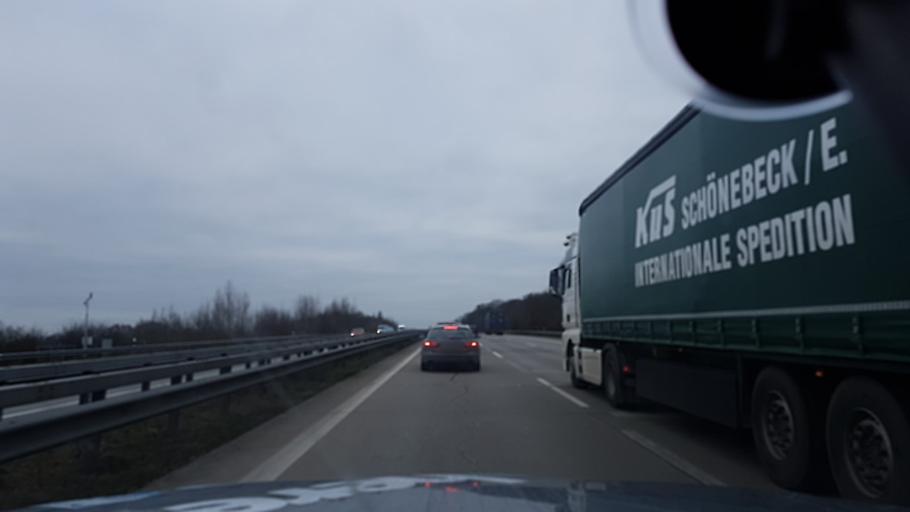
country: DE
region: Schleswig-Holstein
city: Lasbek
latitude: 53.7523
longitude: 10.3696
